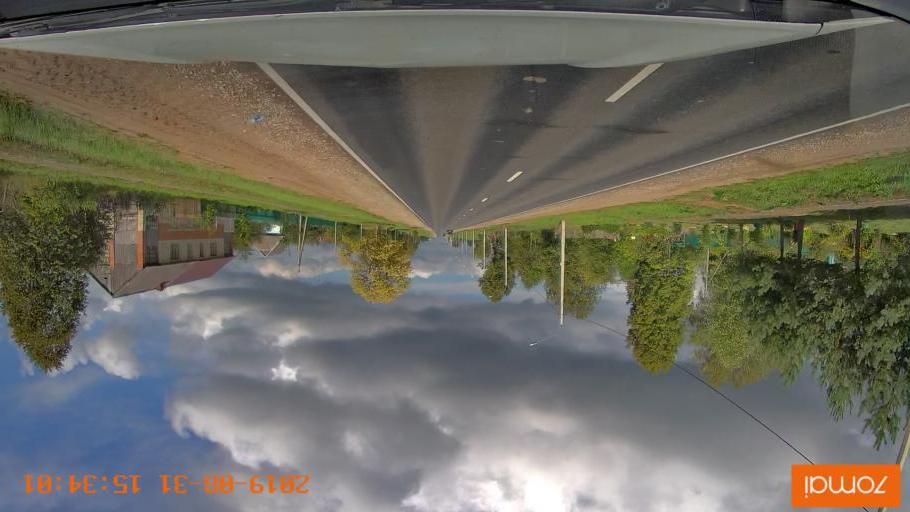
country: RU
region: Kaluga
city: Mosal'sk
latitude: 54.5984
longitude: 34.7125
